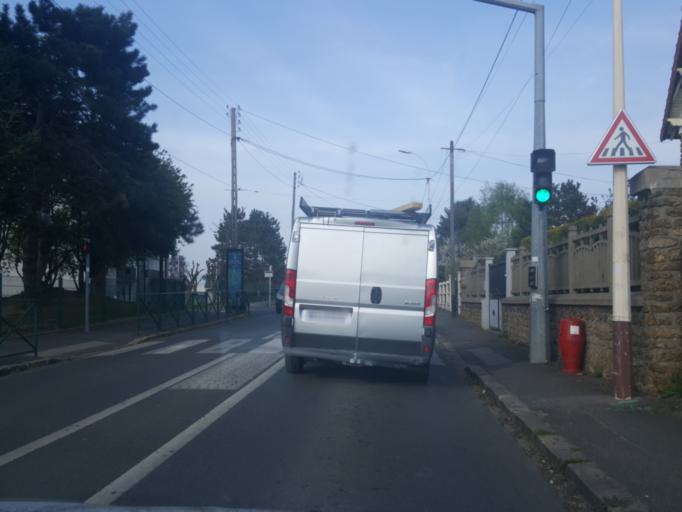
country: FR
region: Ile-de-France
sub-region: Departement de l'Essonne
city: Villiers-sur-Orge
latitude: 48.6486
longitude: 2.3040
